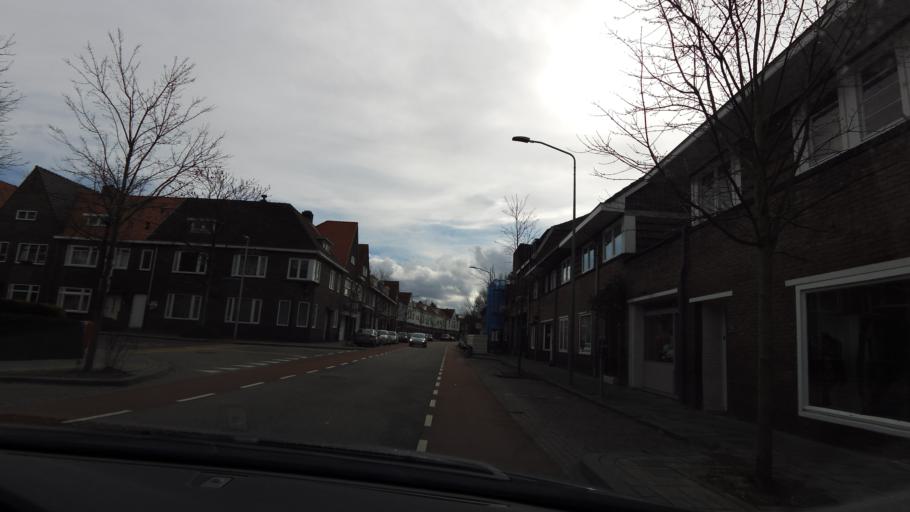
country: NL
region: Limburg
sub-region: Gemeente Heerlen
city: Heerlen
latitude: 50.8795
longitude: 5.9794
